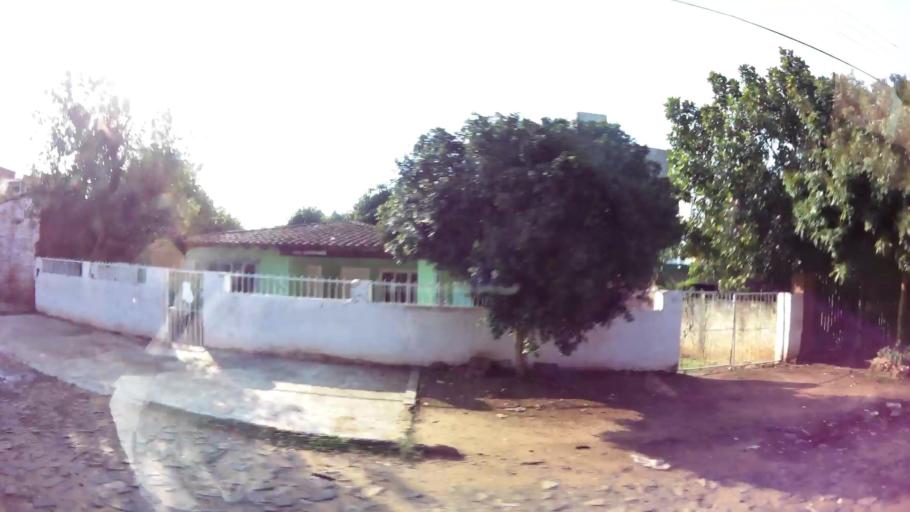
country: PY
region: Central
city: Lambare
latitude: -25.3467
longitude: -57.5885
